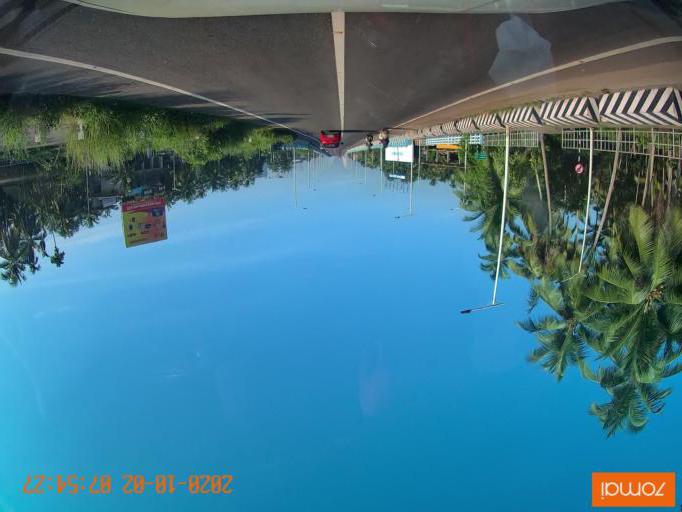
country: IN
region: Kerala
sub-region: Kozhikode
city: Ferokh
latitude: 11.1726
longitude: 75.8743
